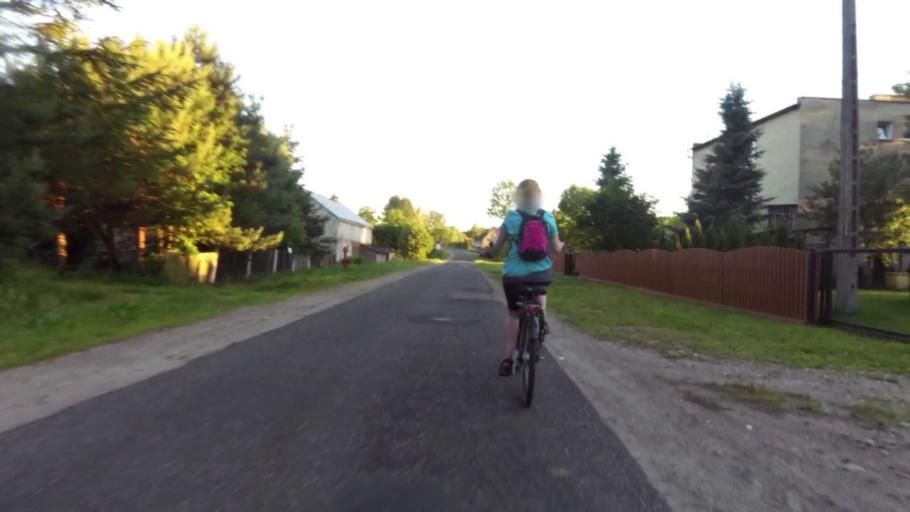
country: PL
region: West Pomeranian Voivodeship
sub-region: Powiat bialogardzki
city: Bialogard
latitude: 54.0422
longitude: 16.0481
